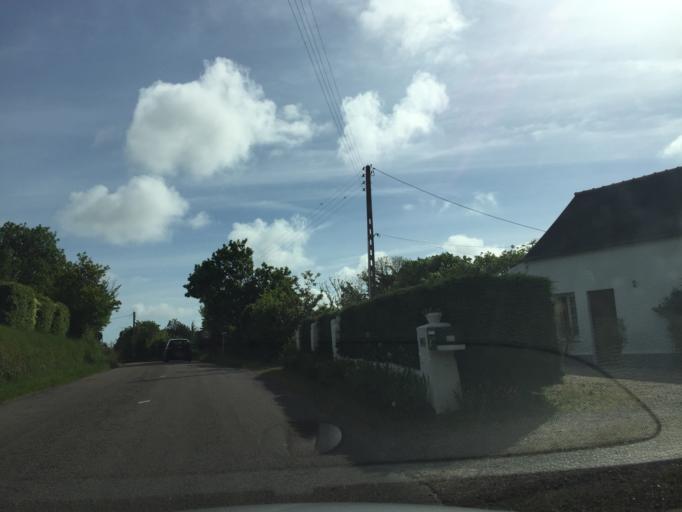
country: FR
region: Brittany
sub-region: Departement des Cotes-d'Armor
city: Matignon
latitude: 48.6301
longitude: -2.3292
